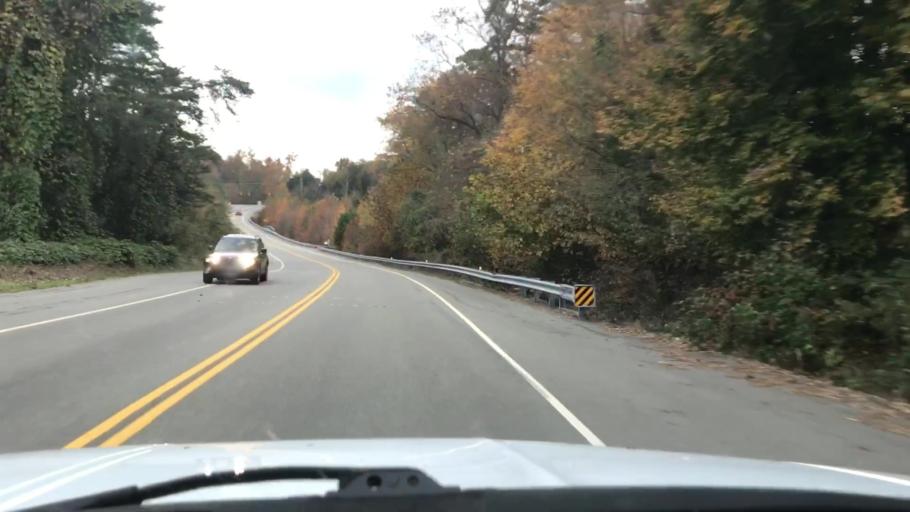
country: US
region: Virginia
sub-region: Goochland County
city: Goochland
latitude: 37.6720
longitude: -77.8787
